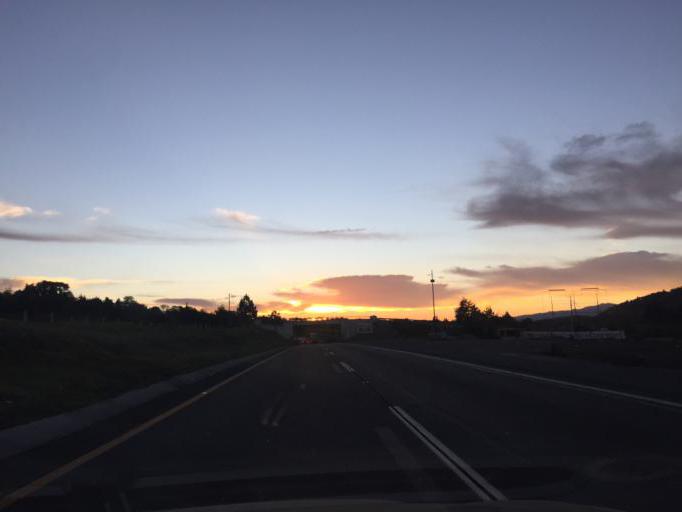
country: MX
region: Puebla
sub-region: Esperanza
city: San Jose Cuyachapa
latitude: 18.8329
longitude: -97.3307
